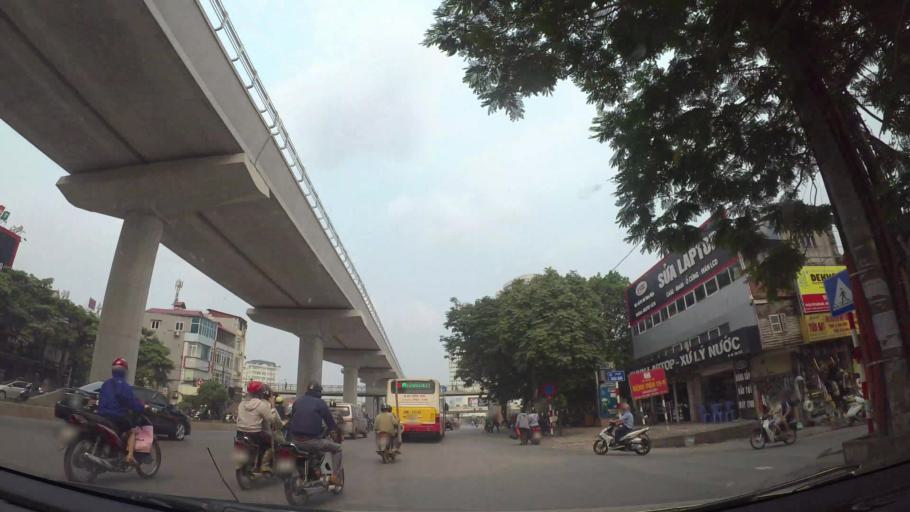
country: VN
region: Ha Noi
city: Cau Dien
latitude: 21.0365
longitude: 105.7787
